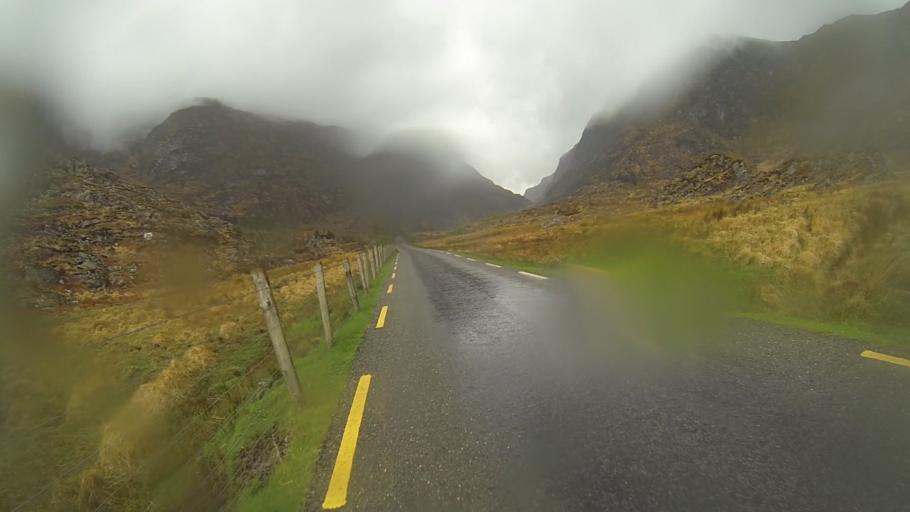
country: IE
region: Munster
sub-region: Ciarrai
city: Cill Airne
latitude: 52.0190
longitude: -9.6359
